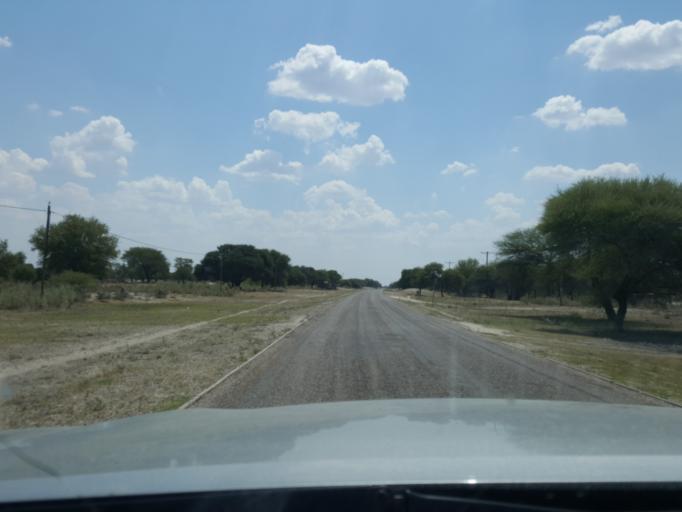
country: BW
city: Tsau
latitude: -20.1780
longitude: 22.4614
